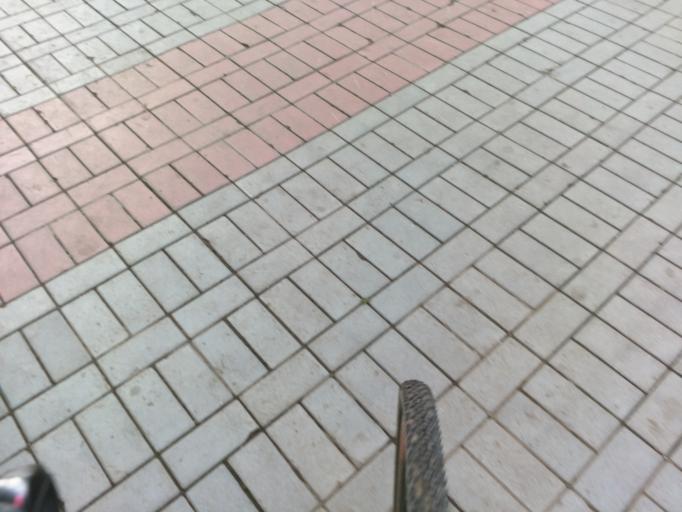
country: RU
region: Tatarstan
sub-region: Tukayevskiy Rayon
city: Naberezhnyye Chelny
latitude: 55.7423
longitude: 52.4132
